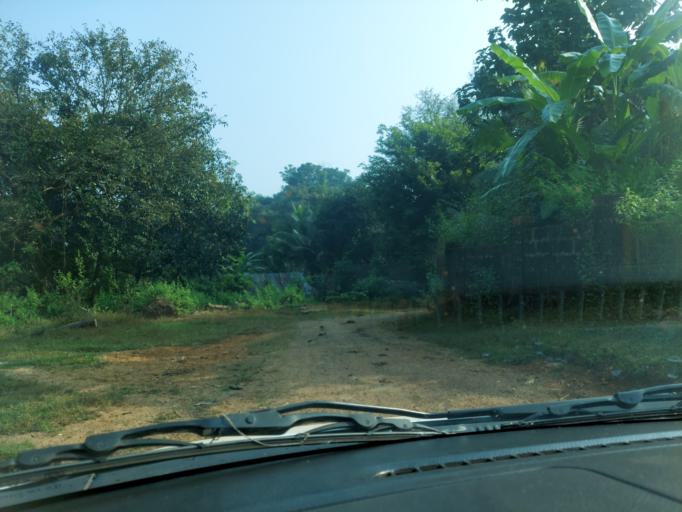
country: IN
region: Maharashtra
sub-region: Sindhudurg
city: Kudal
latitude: 16.0399
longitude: 73.6805
